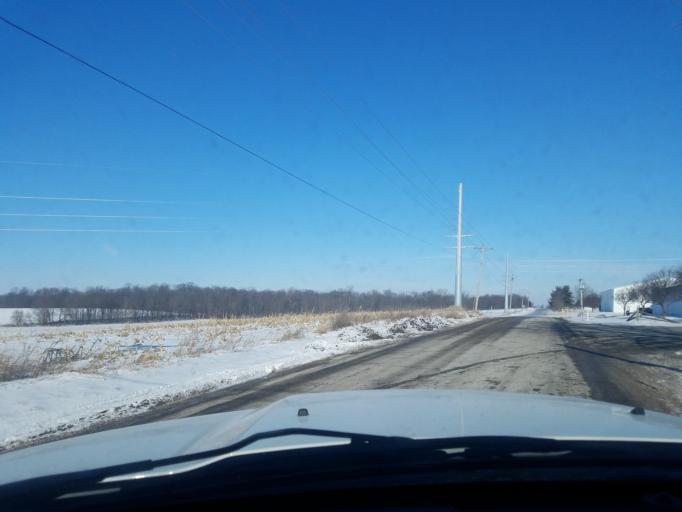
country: US
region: Indiana
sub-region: Noble County
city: Albion
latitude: 41.3961
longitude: -85.3956
